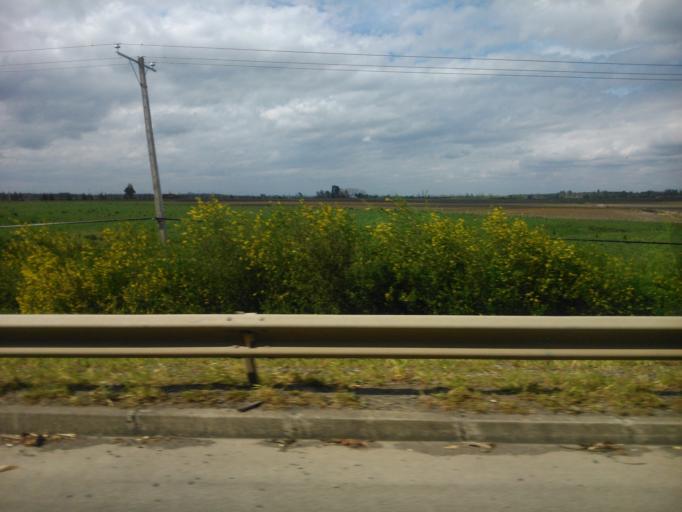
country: CL
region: Biobio
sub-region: Provincia de Nuble
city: Bulnes
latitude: -36.7785
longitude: -72.3131
